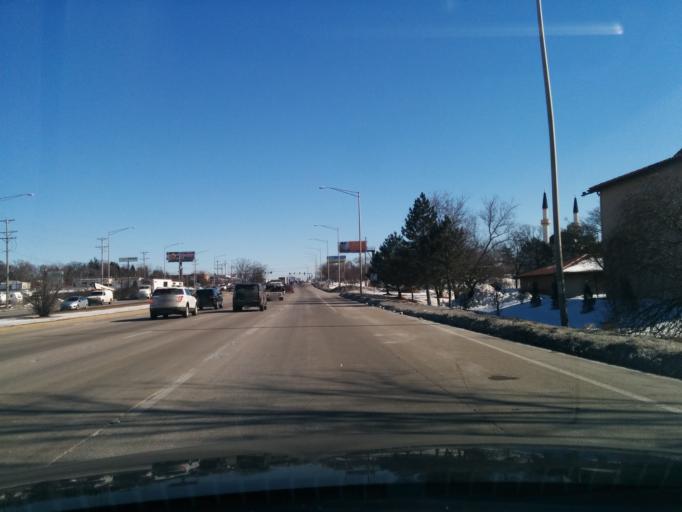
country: US
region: Illinois
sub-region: DuPage County
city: Glendale Heights
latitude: 41.9037
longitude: -88.0477
